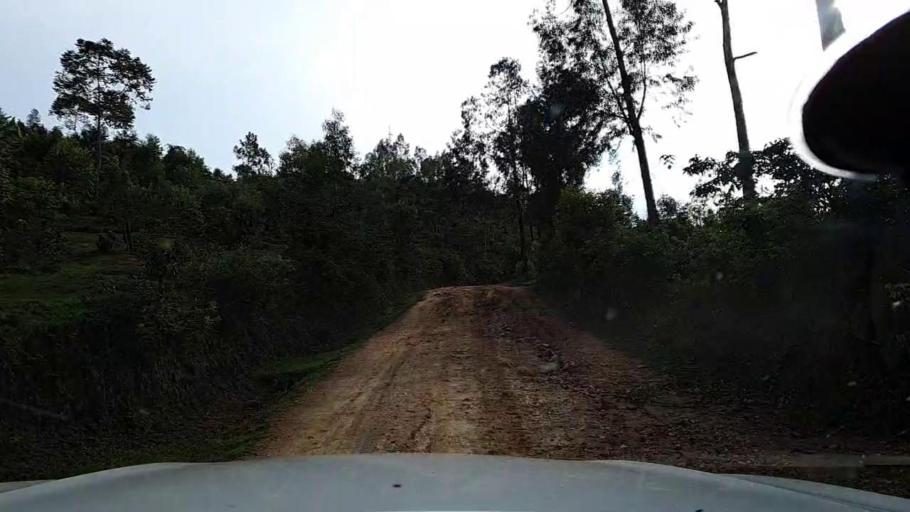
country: RW
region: Southern Province
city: Gitarama
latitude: -2.1678
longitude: 29.5570
